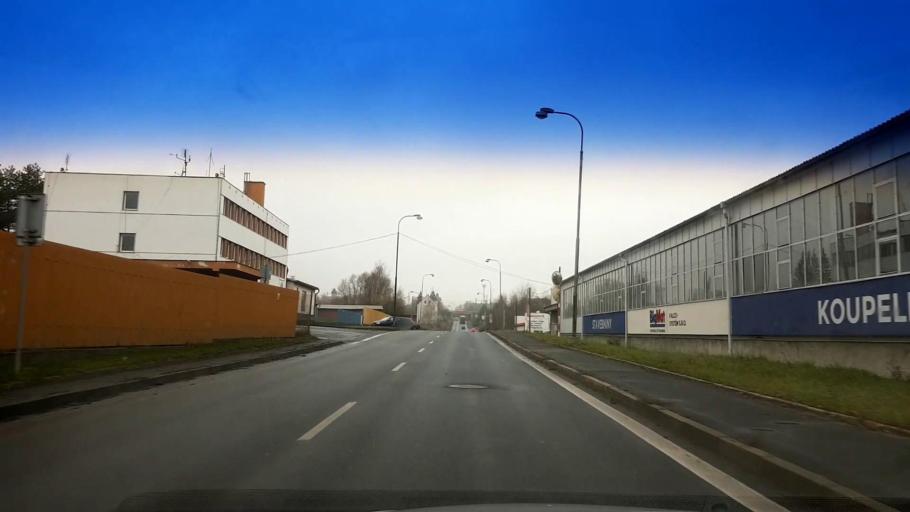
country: CZ
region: Karlovarsky
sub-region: Okres Cheb
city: Cheb
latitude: 50.0763
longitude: 12.3895
